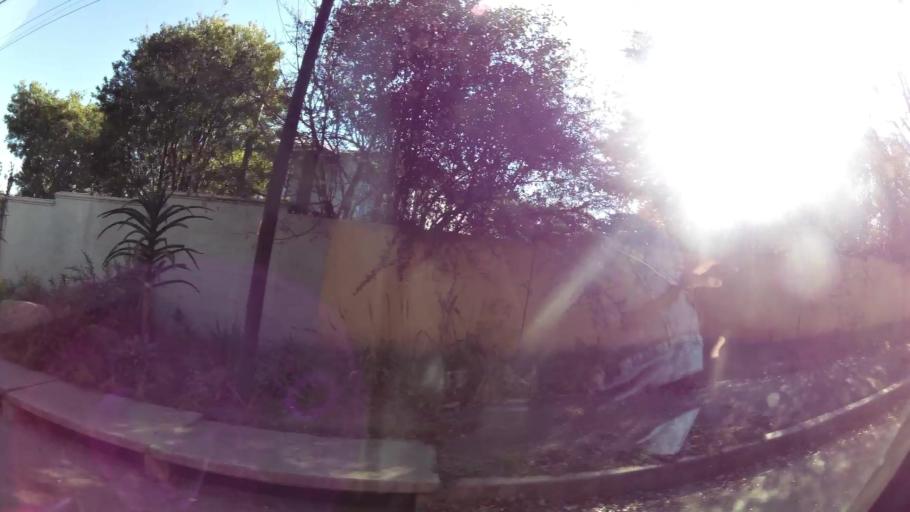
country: ZA
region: Gauteng
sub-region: City of Johannesburg Metropolitan Municipality
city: Johannesburg
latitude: -26.1247
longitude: 28.0173
